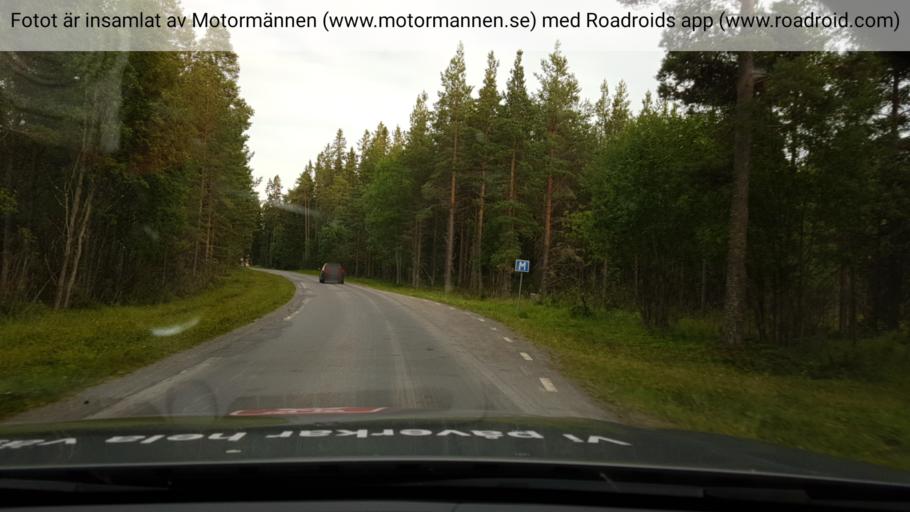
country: SE
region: Jaemtland
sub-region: Krokoms Kommun
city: Krokom
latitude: 63.1326
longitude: 14.4207
